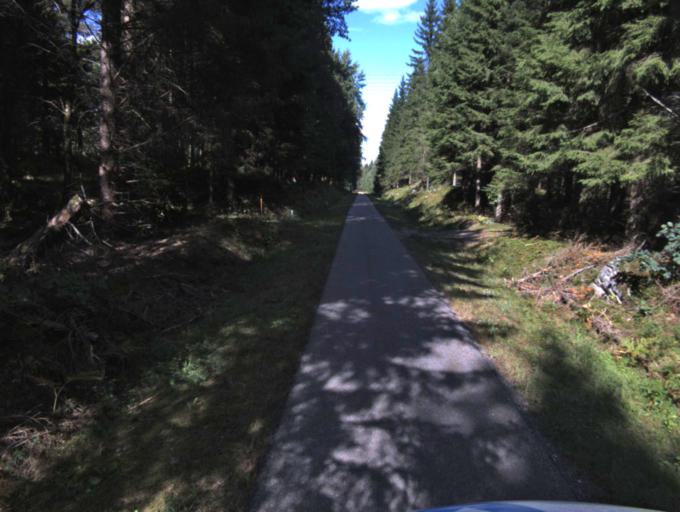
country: SE
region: Vaestra Goetaland
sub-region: Ulricehamns Kommun
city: Ulricehamn
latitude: 57.8252
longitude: 13.3459
